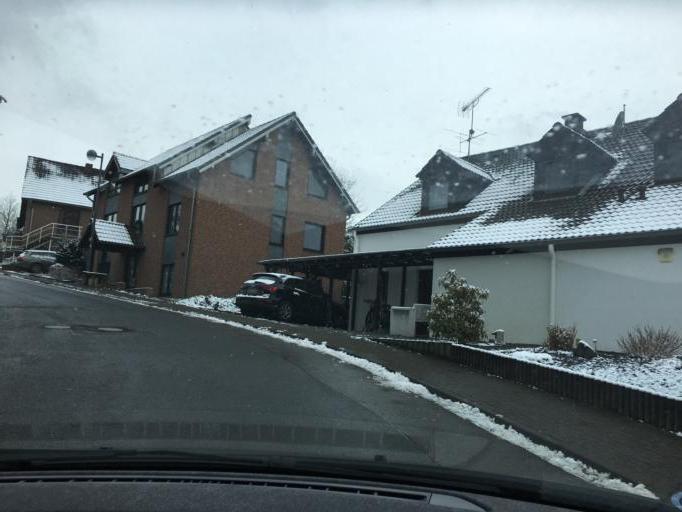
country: DE
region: North Rhine-Westphalia
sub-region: Regierungsbezirk Koln
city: Nideggen
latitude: 50.7186
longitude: 6.4376
